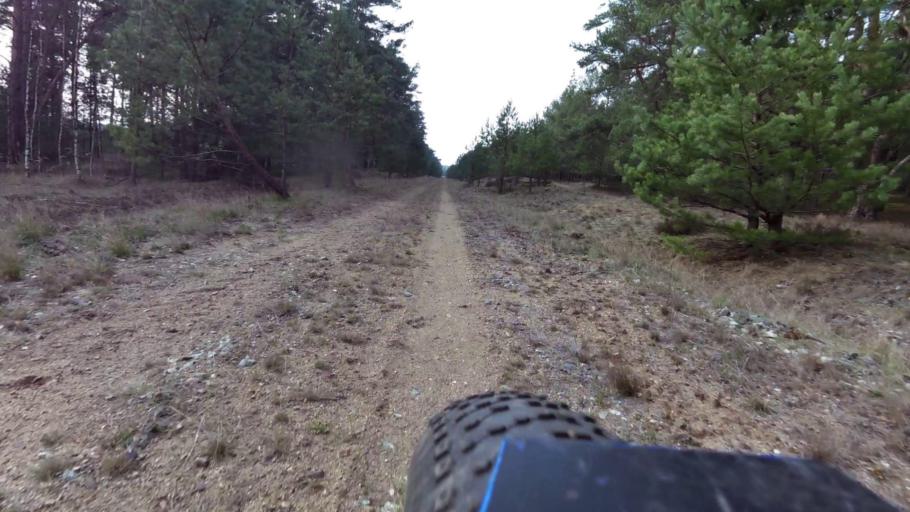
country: PL
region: Lubusz
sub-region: Powiat slubicki
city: Cybinka
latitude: 52.2448
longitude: 14.7607
